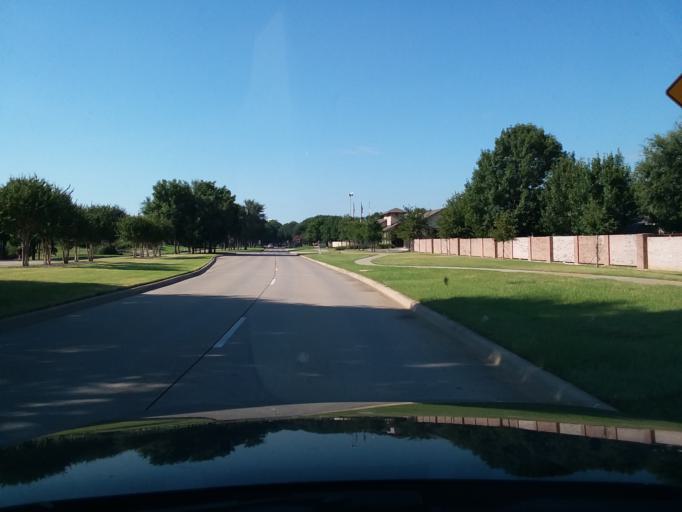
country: US
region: Texas
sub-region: Denton County
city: Double Oak
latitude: 33.0501
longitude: -97.0934
